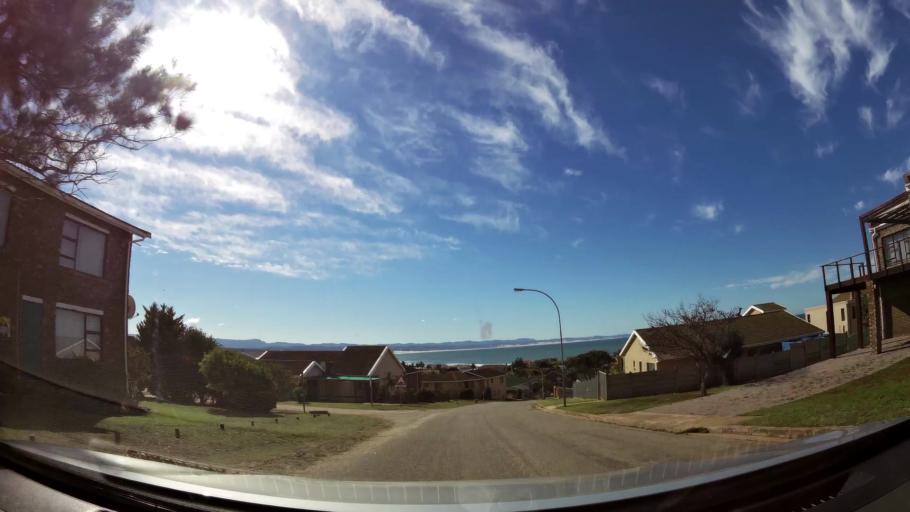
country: ZA
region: Eastern Cape
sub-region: Cacadu District Municipality
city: Jeffrey's Bay
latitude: -34.0189
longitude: 24.9235
